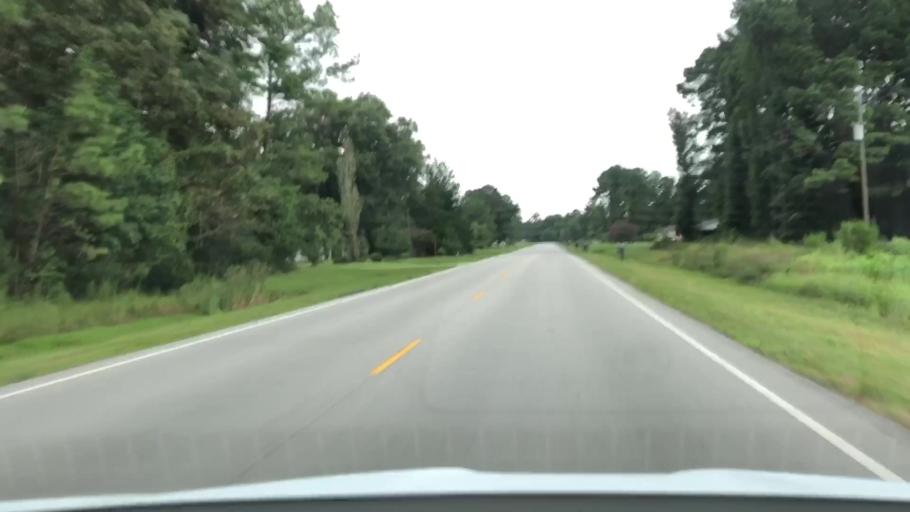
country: US
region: North Carolina
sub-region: Jones County
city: Trenton
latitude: 35.0225
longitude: -77.3052
